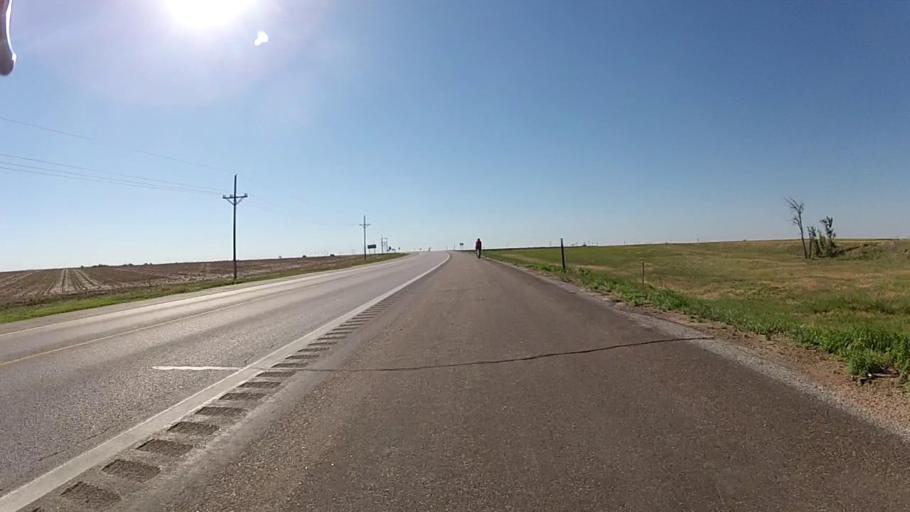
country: US
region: Kansas
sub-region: Ford County
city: Dodge City
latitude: 37.5882
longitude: -99.6852
